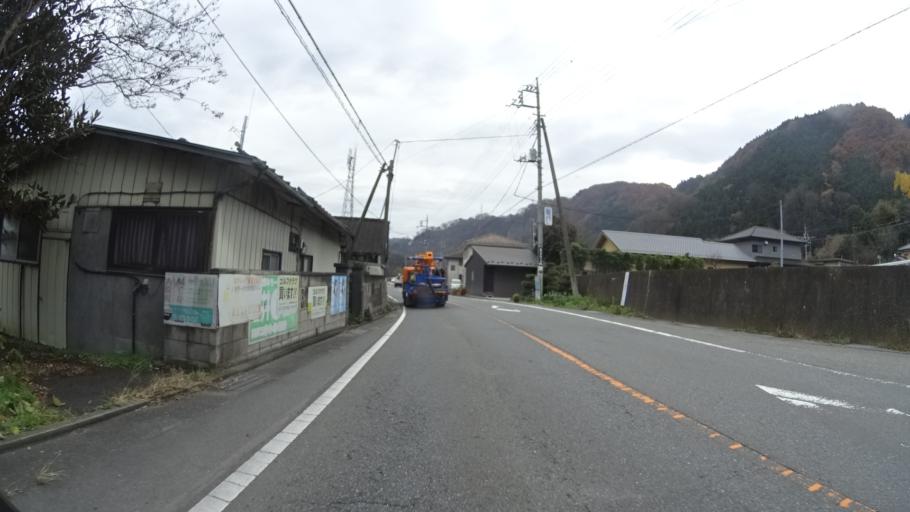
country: JP
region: Gunma
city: Numata
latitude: 36.5993
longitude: 139.0493
